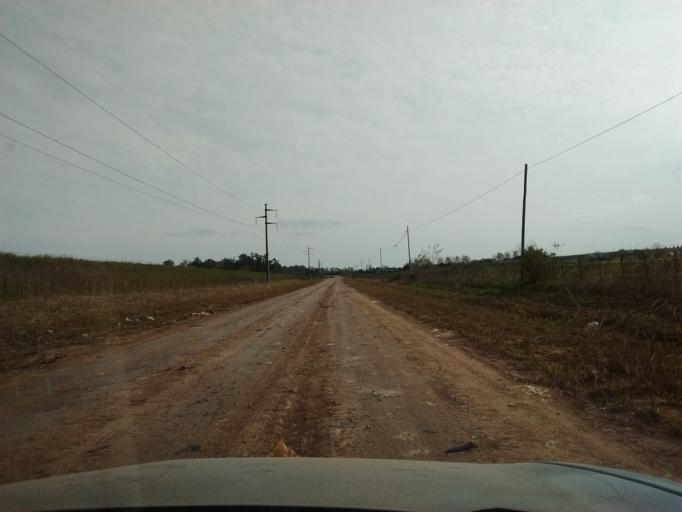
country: AR
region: Santa Fe
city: Funes
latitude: -32.9425
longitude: -60.8123
